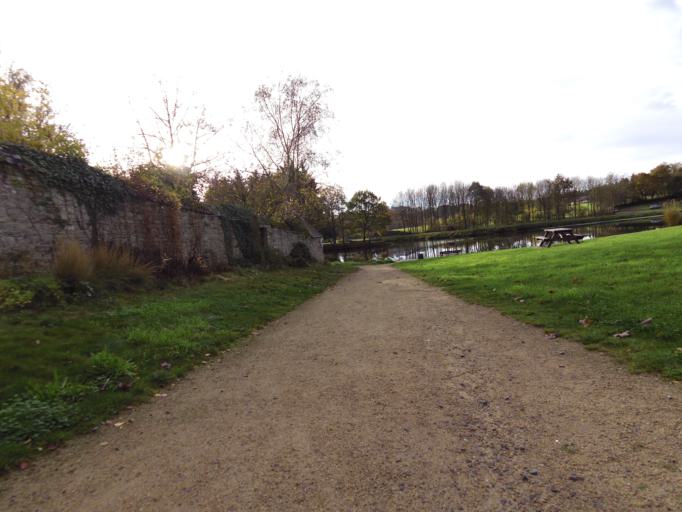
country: FR
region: Brittany
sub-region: Departement d'Ille-et-Vilaine
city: Bourg-des-Comptes
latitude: 47.9276
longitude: -1.7499
